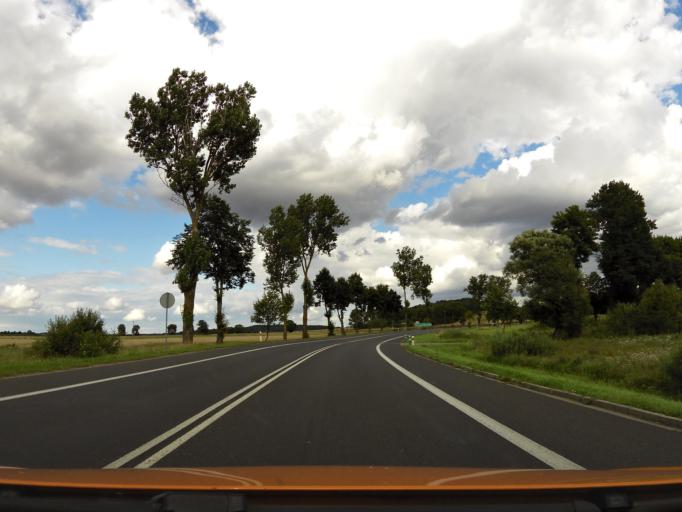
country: PL
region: West Pomeranian Voivodeship
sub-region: Powiat kolobrzeski
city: Ryman
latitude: 53.9291
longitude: 15.4825
